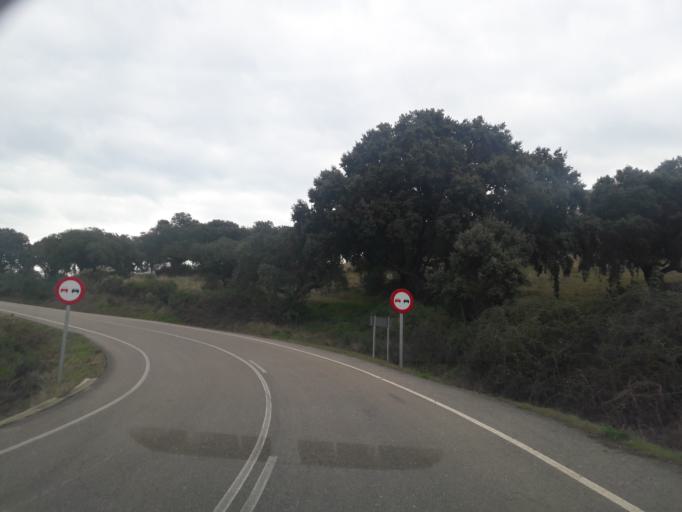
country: ES
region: Castille and Leon
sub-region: Provincia de Salamanca
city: Serradilla del Arroyo
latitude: 40.5186
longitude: -6.3984
